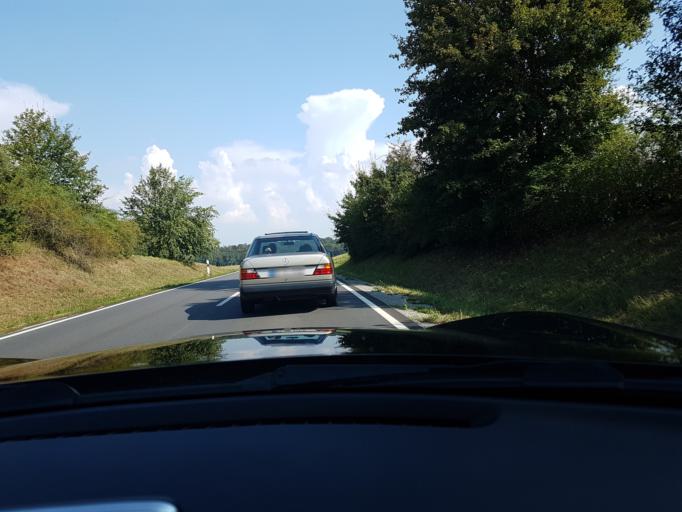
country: DE
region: Baden-Wuerttemberg
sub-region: Karlsruhe Region
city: Seckach
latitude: 49.4765
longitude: 9.3762
